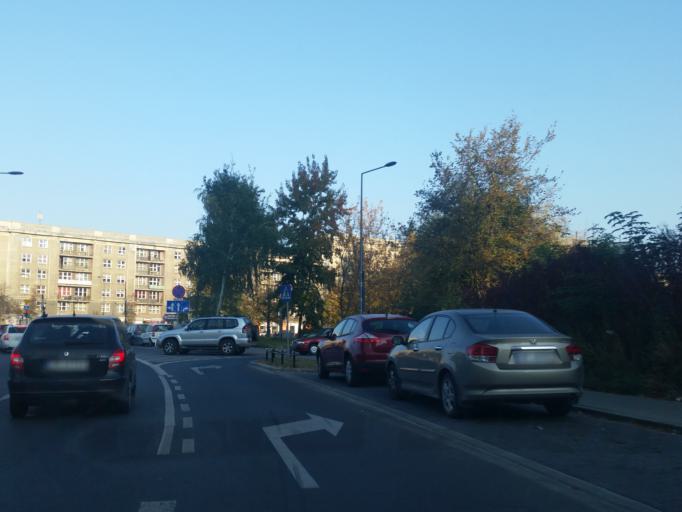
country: PL
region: Masovian Voivodeship
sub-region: Warszawa
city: Mokotow
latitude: 52.1830
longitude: 21.0253
